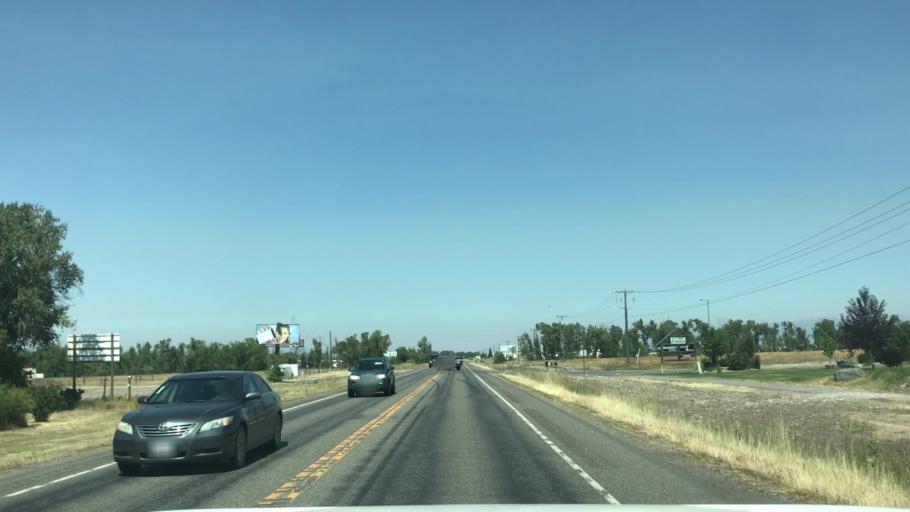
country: US
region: Montana
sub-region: Gallatin County
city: Four Corners
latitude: 45.5940
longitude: -111.1969
